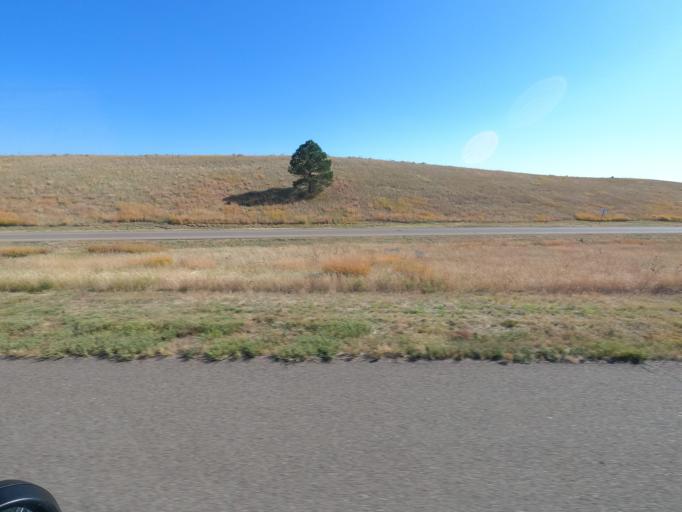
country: US
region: Nebraska
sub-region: Deuel County
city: Chappell
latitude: 40.9032
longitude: -102.5158
